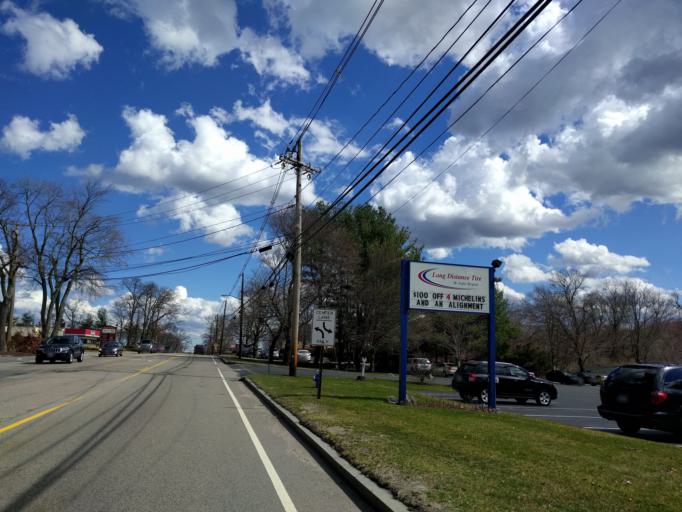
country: US
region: Massachusetts
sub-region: Norfolk County
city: Medway
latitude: 42.1501
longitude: -71.4162
